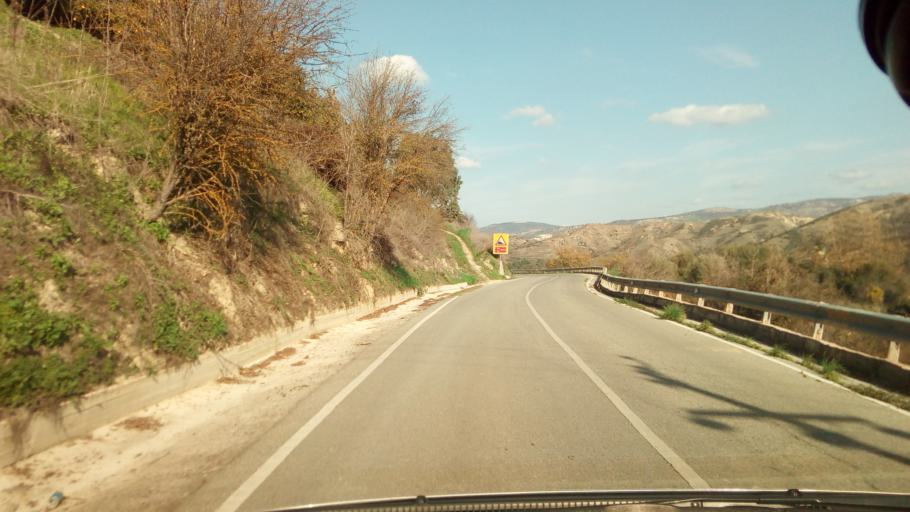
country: CY
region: Pafos
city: Pegeia
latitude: 34.9355
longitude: 32.4671
